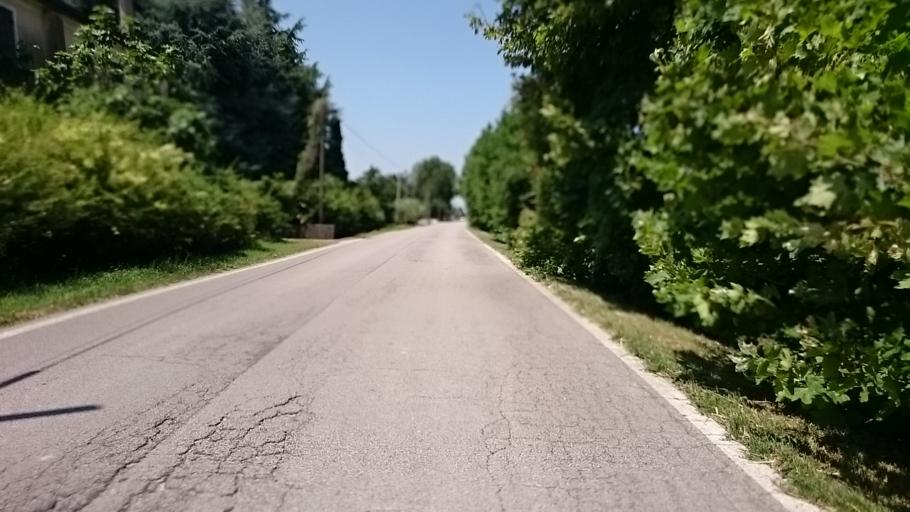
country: IT
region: Veneto
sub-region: Provincia di Venezia
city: Sant'Angelo
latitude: 45.5176
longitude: 12.0004
